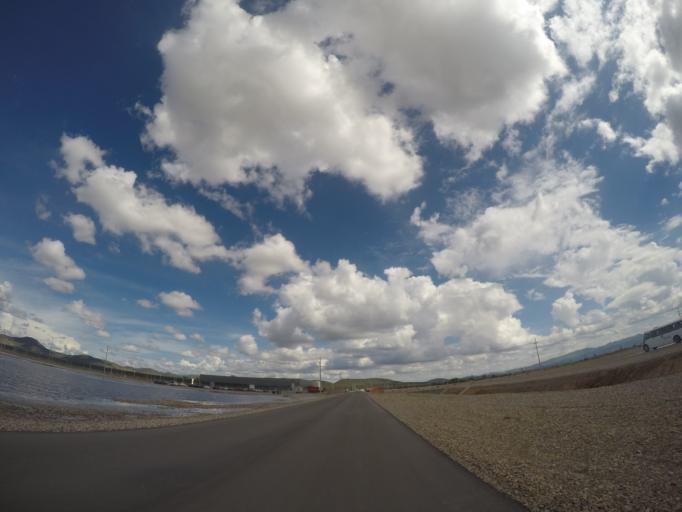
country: MX
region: San Luis Potosi
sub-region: Zaragoza
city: Cerro Gordo
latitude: 21.9651
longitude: -100.8462
